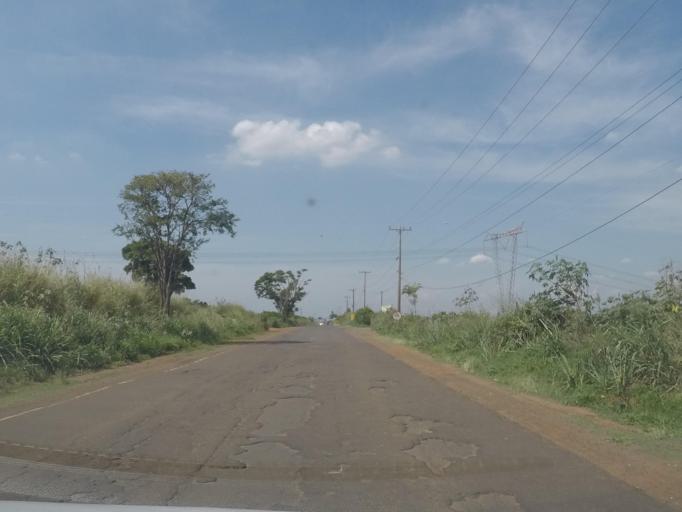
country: BR
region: Sao Paulo
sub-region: Sumare
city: Sumare
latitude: -22.8656
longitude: -47.2954
